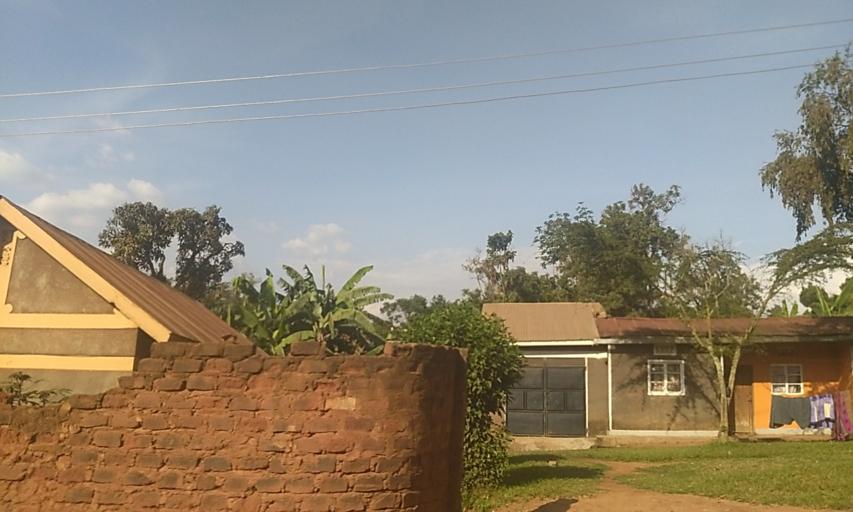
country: UG
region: Central Region
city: Kampala Central Division
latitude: 0.3224
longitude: 32.5432
